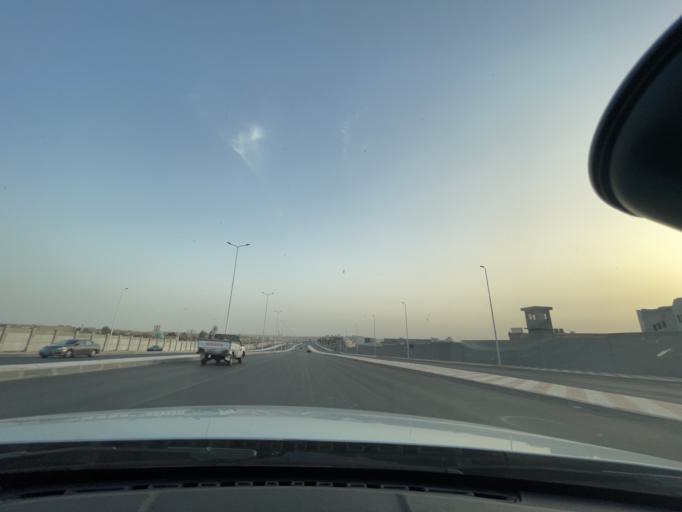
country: EG
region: Muhafazat al Qahirah
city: Cairo
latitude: 30.0321
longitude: 31.3512
